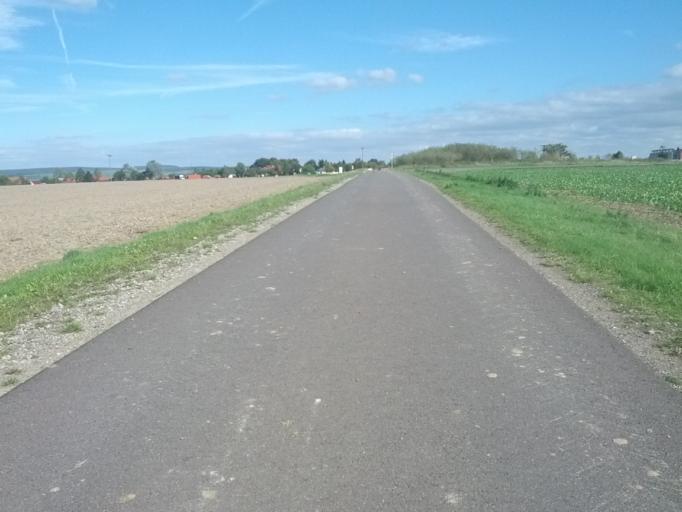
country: DE
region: Thuringia
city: Eisenach
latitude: 51.0183
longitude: 10.3273
